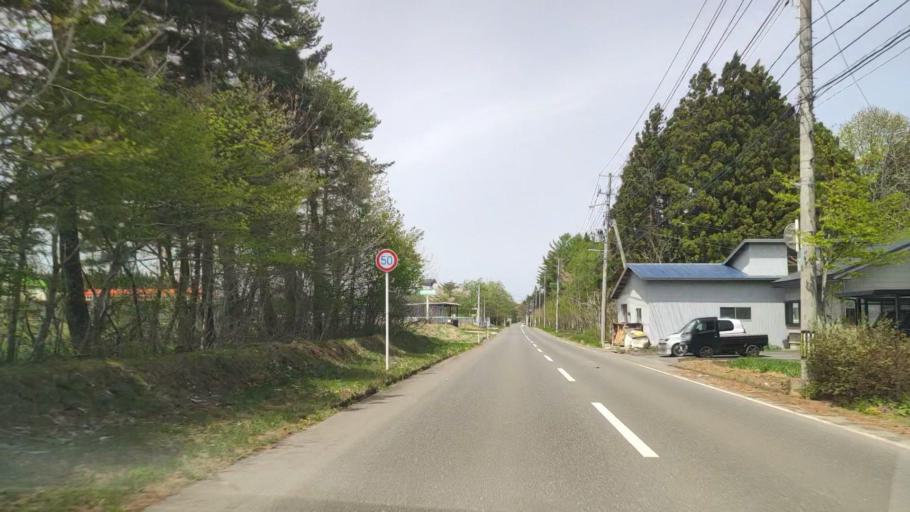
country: JP
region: Aomori
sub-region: Misawa Shi
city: Inuotose
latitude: 40.7170
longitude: 141.1432
